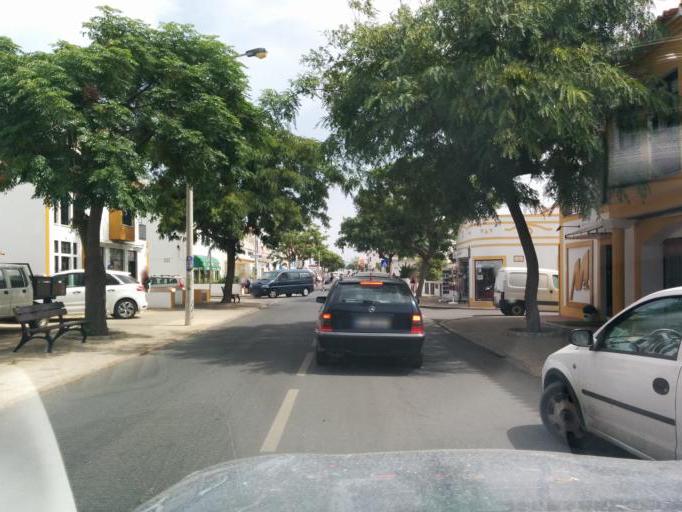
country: PT
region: Beja
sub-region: Odemira
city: Vila Nova de Milfontes
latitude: 37.7269
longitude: -8.7790
